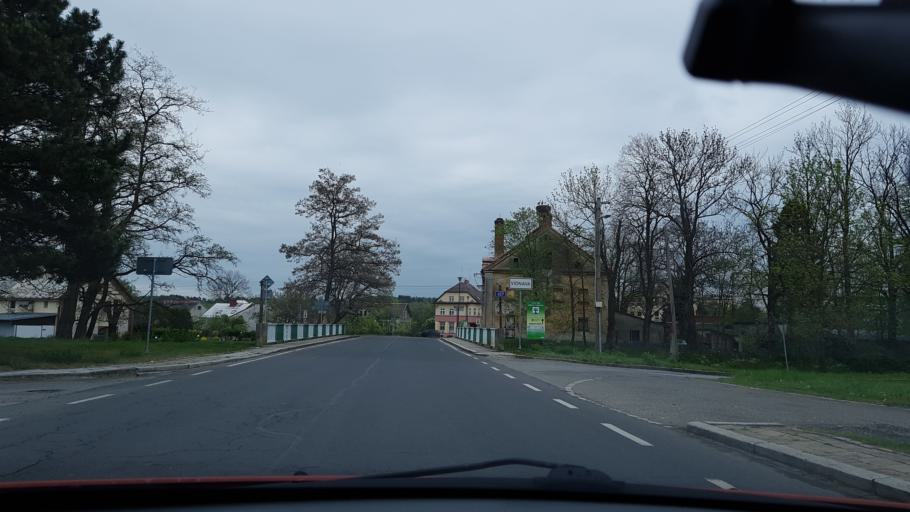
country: CZ
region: Olomoucky
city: Vidnava
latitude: 50.3737
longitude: 17.1819
